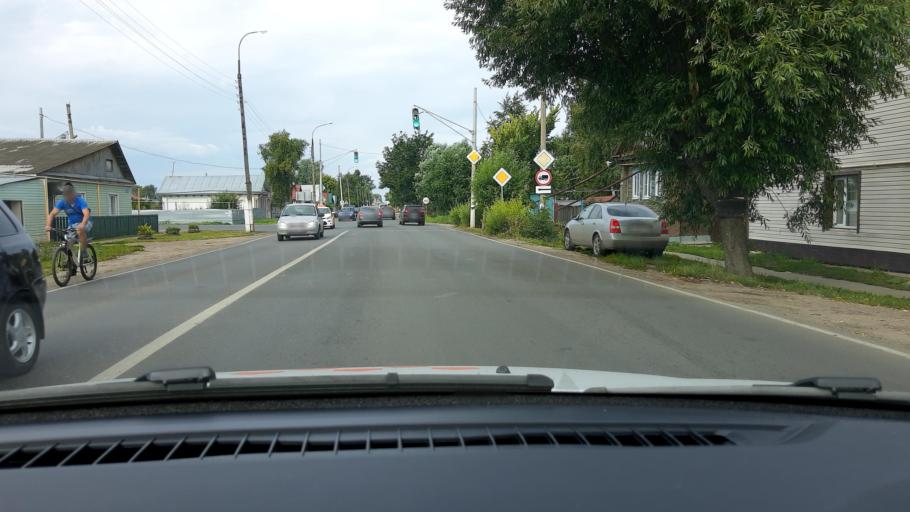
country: RU
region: Nizjnij Novgorod
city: Vyyezdnoye
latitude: 55.3832
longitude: 43.7897
